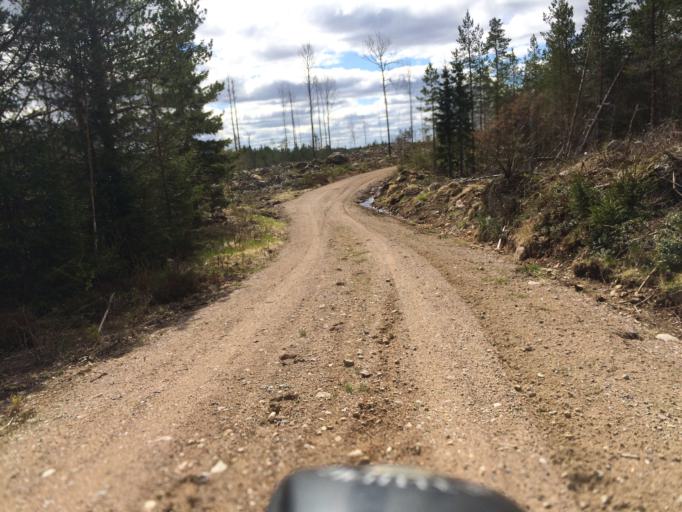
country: SE
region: OErebro
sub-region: Hallefors Kommun
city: Haellefors
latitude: 60.0552
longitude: 14.5216
